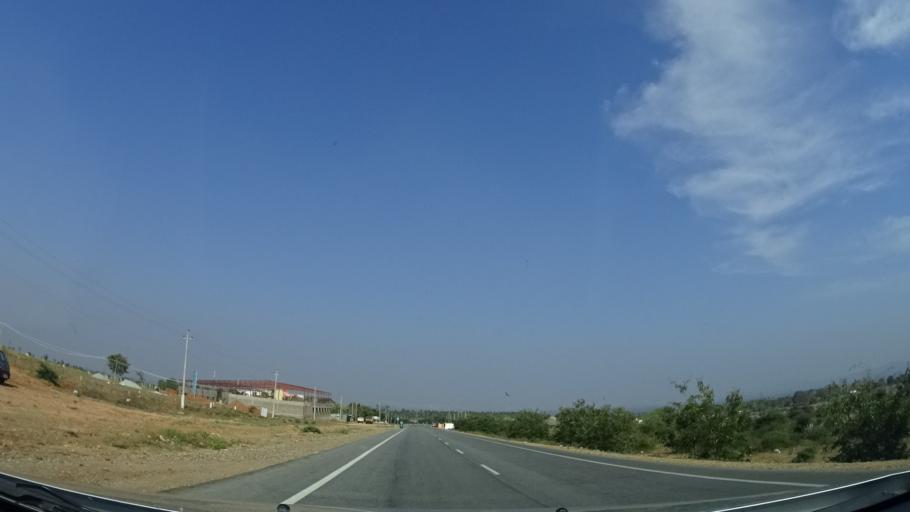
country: IN
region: Karnataka
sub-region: Chamrajnagar
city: Gundlupet
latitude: 11.8009
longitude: 76.6710
